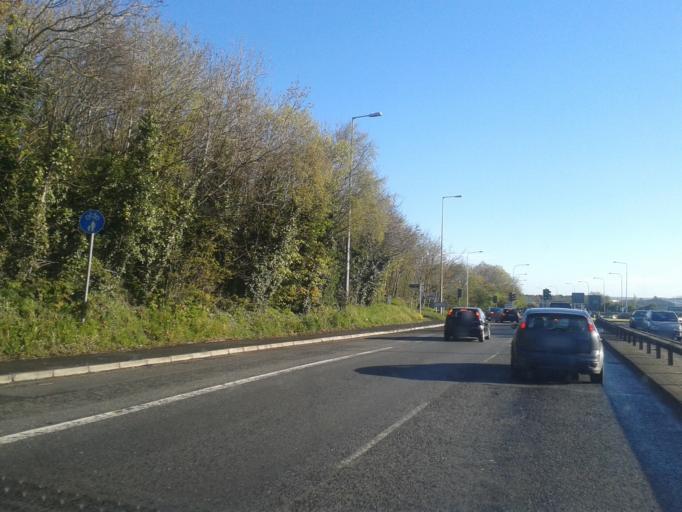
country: IE
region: Leinster
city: Kinsealy-Drinan
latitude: 53.4332
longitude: -6.2296
